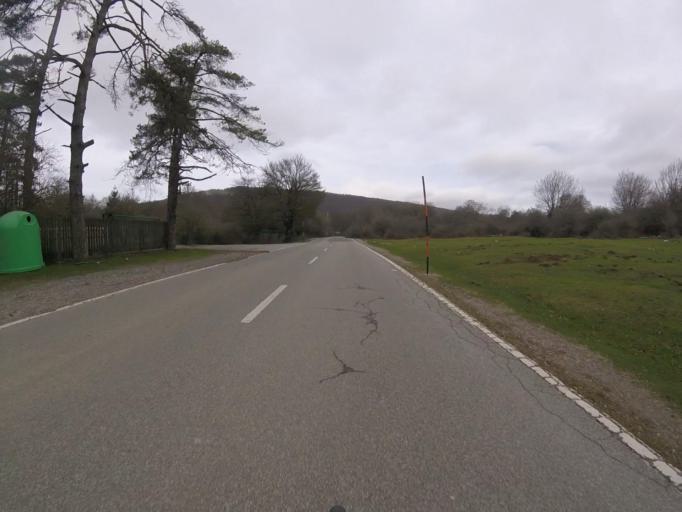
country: ES
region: Navarre
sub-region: Provincia de Navarra
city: Olazagutia
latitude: 42.8519
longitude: -2.1716
